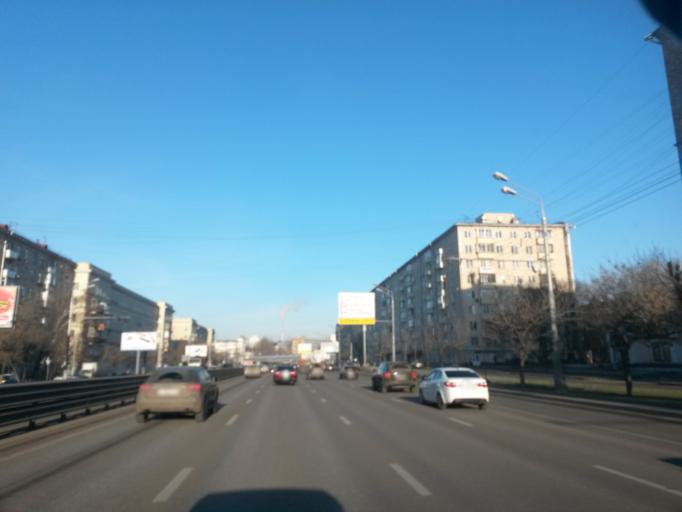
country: RU
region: Moscow
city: Nagornyy
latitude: 55.6590
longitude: 37.6196
